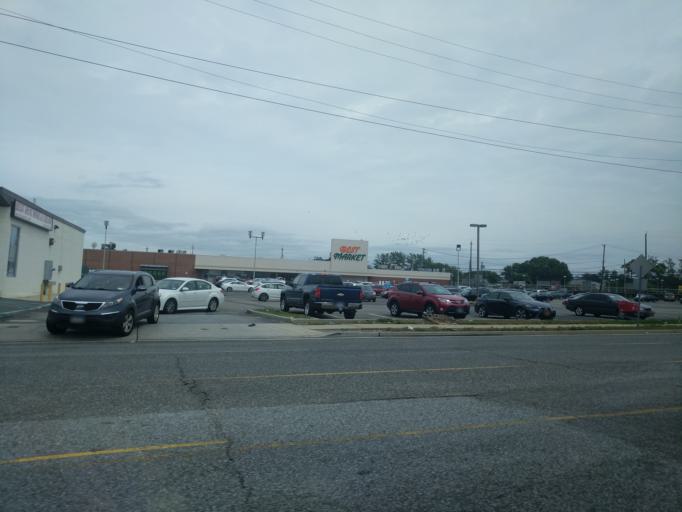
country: US
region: New York
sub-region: Nassau County
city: East Rockaway
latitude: 40.6407
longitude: -73.6589
